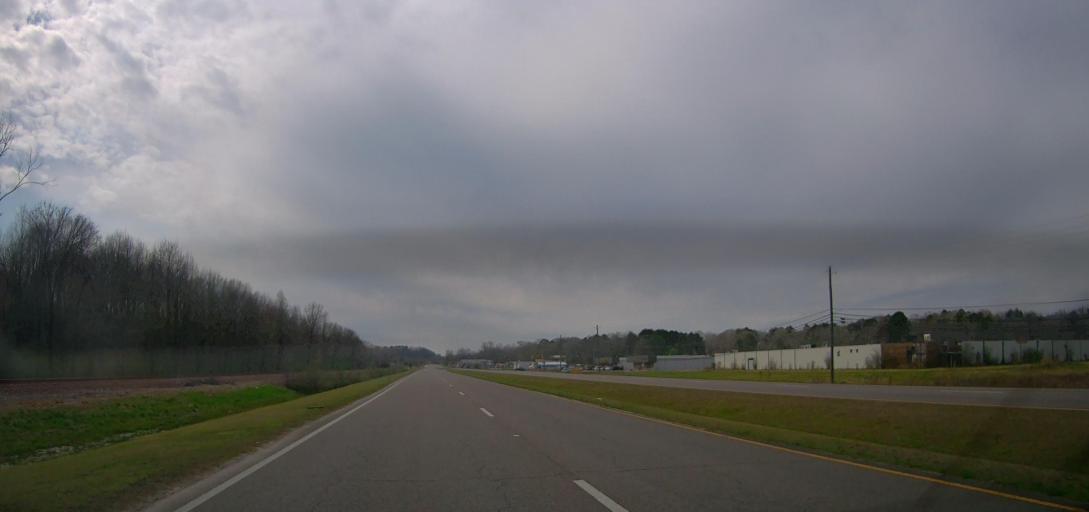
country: US
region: Alabama
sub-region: Walker County
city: Carbon Hill
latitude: 33.8844
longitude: -87.5176
